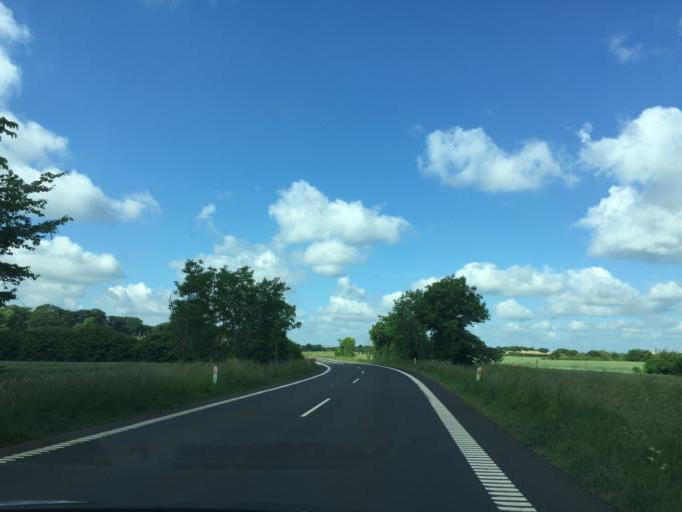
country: DK
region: South Denmark
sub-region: Fredericia Kommune
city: Taulov
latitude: 55.5328
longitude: 9.6612
